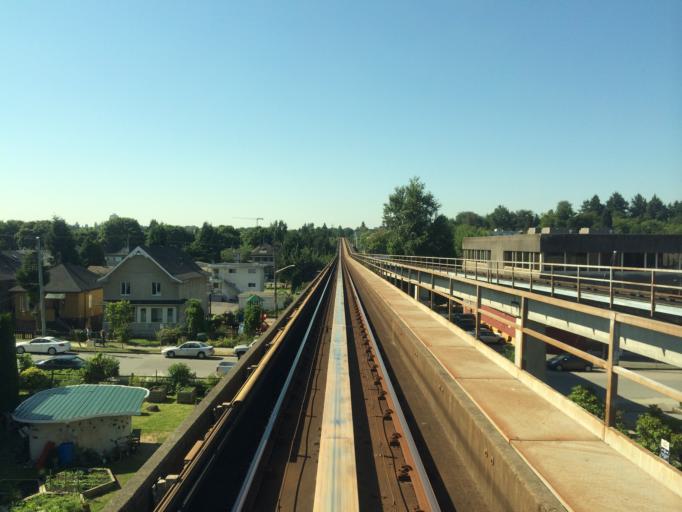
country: CA
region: British Columbia
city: Vancouver
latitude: 49.2608
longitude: -123.0691
